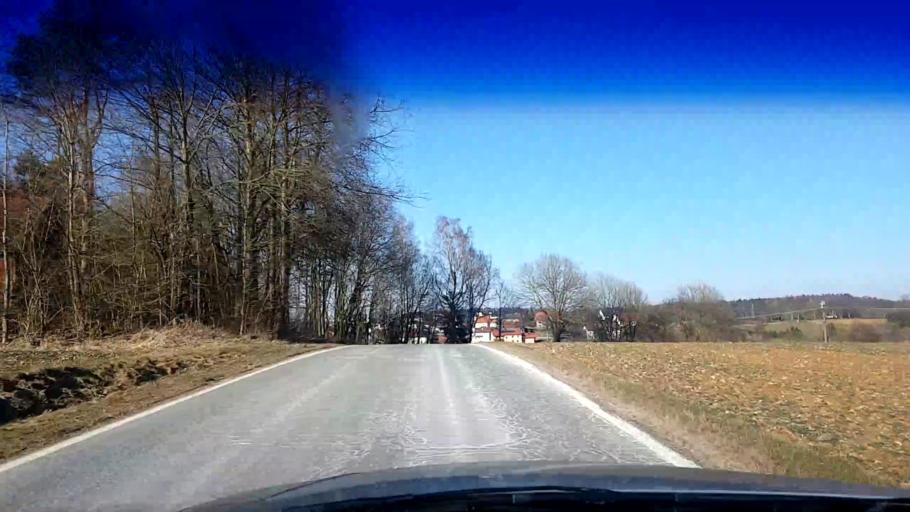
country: DE
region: Bavaria
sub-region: Upper Franconia
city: Aufsess
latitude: 49.9230
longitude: 11.2188
